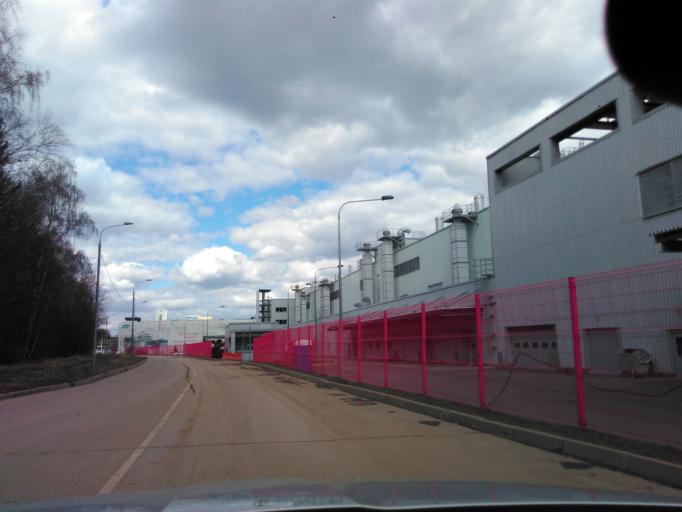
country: RU
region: Moscow
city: Zelenograd
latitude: 55.9780
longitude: 37.2131
